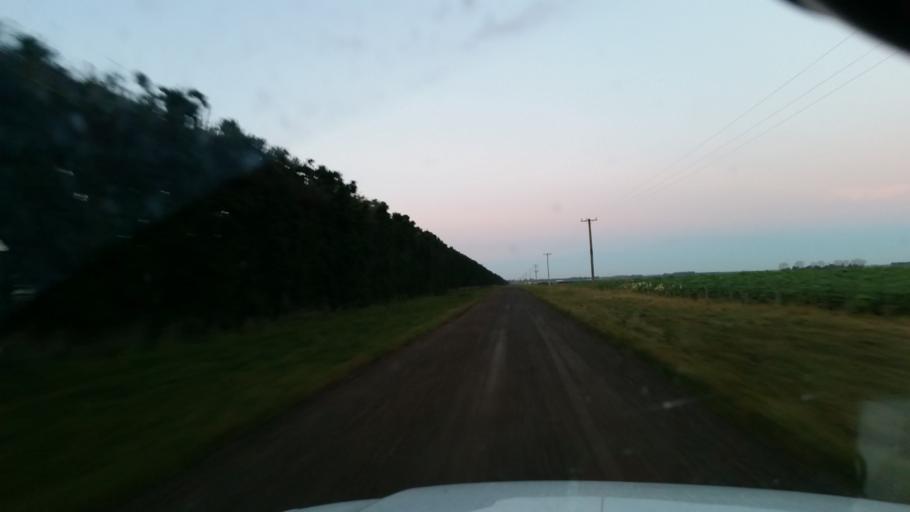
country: NZ
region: Canterbury
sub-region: Ashburton District
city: Tinwald
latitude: -43.9377
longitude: 171.5664
